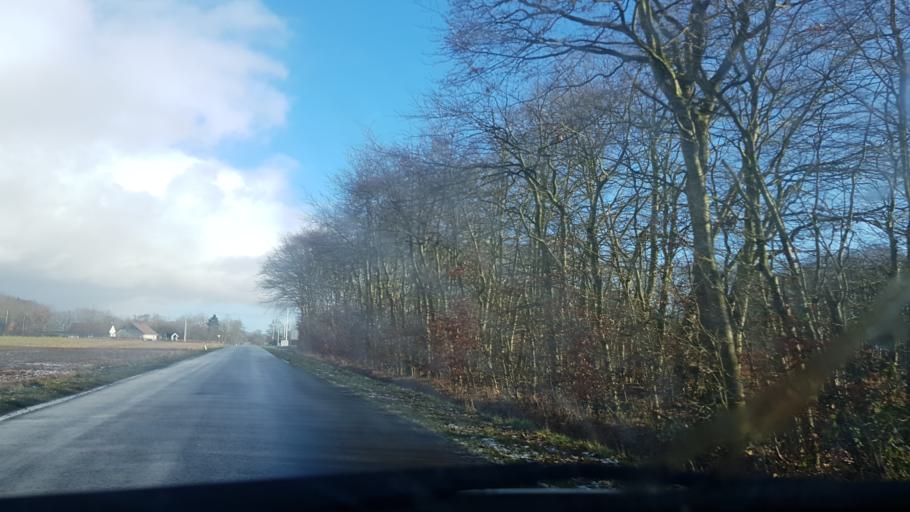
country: DK
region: South Denmark
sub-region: Haderslev Kommune
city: Vojens
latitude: 55.3220
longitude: 9.2462
